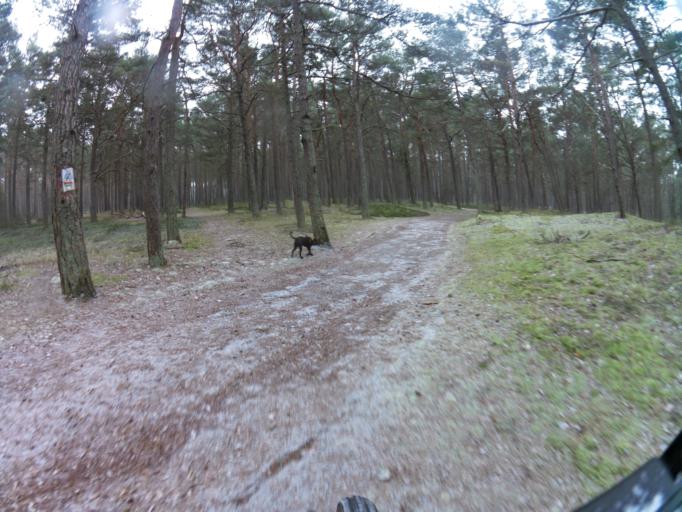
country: PL
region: West Pomeranian Voivodeship
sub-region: Powiat gryficki
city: Cerkwica
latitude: 54.1067
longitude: 15.1325
